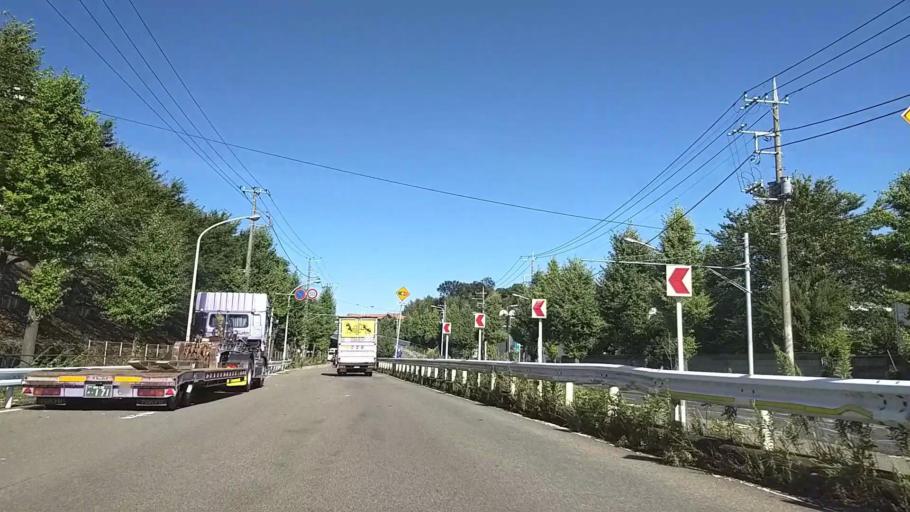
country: JP
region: Tokyo
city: Chofugaoka
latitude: 35.5803
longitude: 139.6103
